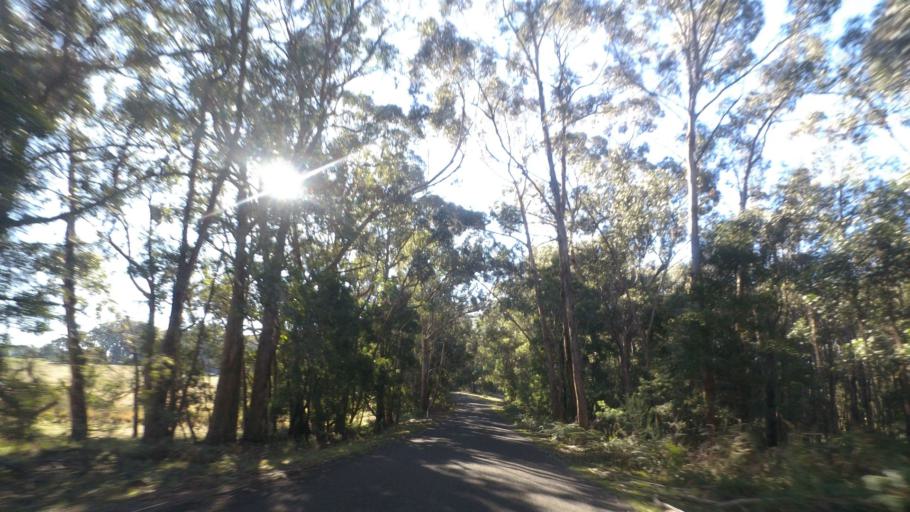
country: AU
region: Victoria
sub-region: Mount Alexander
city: Castlemaine
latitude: -37.3324
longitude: 144.3197
